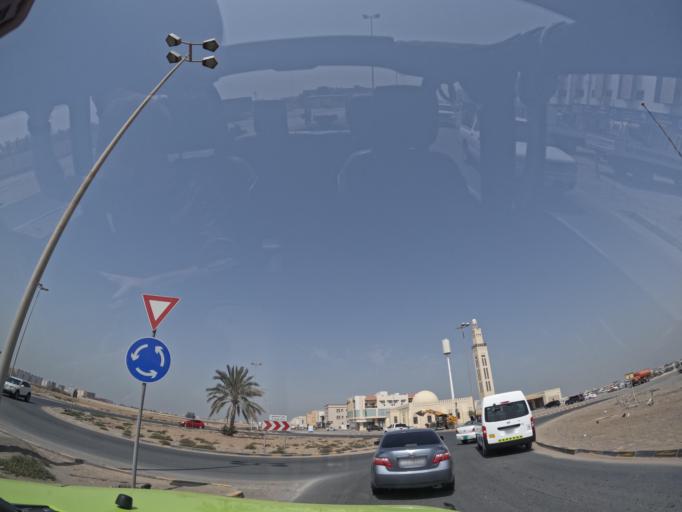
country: AE
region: Umm al Qaywayn
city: Umm al Qaywayn
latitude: 25.5123
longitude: 55.5576
